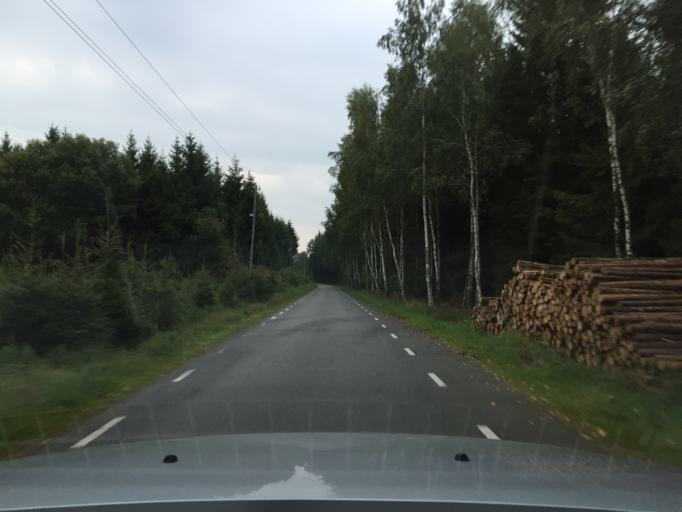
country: SE
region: Skane
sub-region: Hassleholms Kommun
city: Sosdala
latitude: 56.0169
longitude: 13.7306
